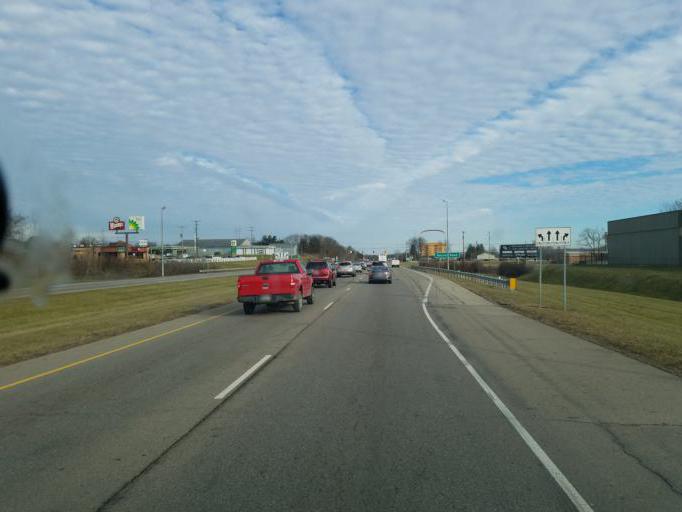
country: US
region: Ohio
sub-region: Licking County
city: Newark
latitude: 40.0632
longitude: -82.3582
